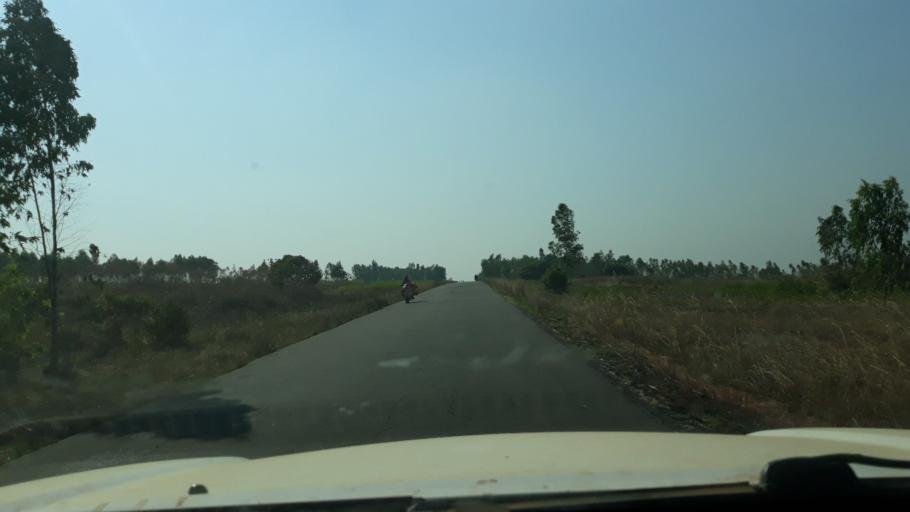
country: BI
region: Cibitoke
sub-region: Commune of Buganda
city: Buganda
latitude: -3.0439
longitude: 29.1142
